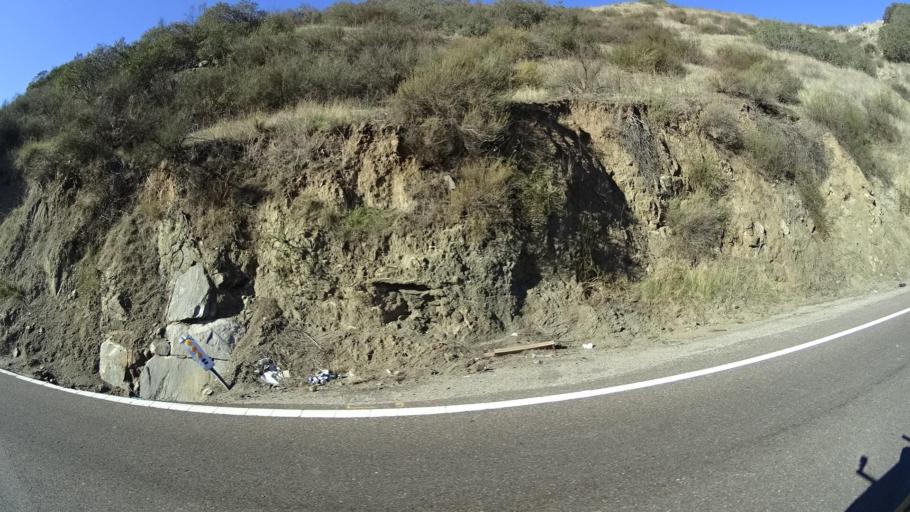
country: US
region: California
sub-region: San Diego County
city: Jamul
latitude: 32.6484
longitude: -116.7864
